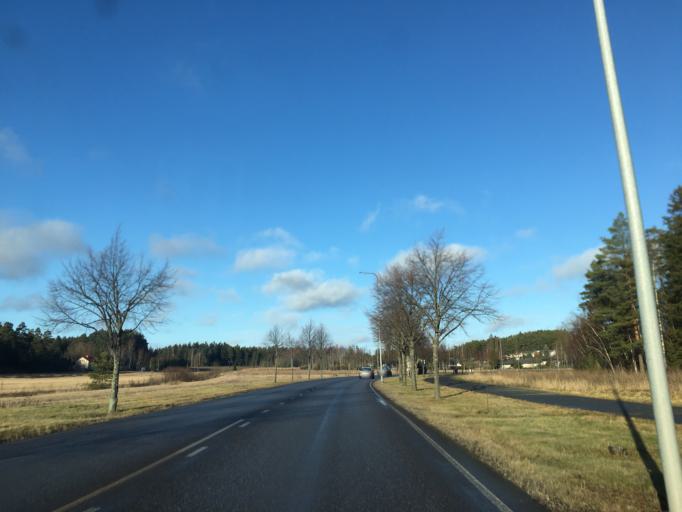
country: FI
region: Varsinais-Suomi
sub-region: Turku
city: Raisio
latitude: 60.4943
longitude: 22.1387
